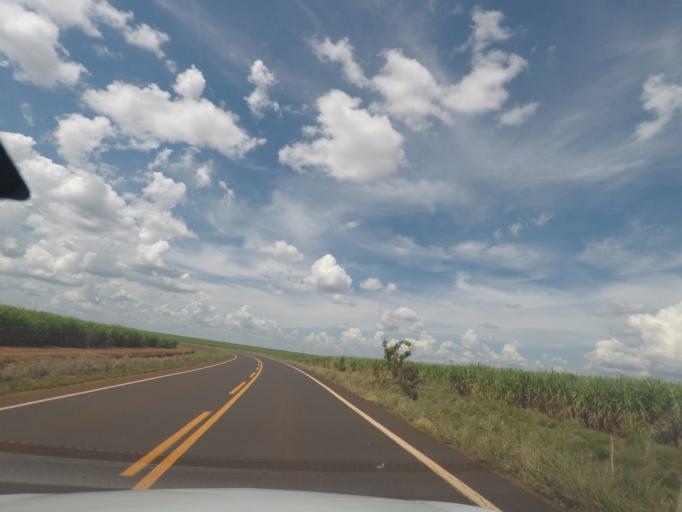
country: BR
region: Minas Gerais
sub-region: Conceicao Das Alagoas
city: Conceicao das Alagoas
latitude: -19.8618
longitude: -48.6028
